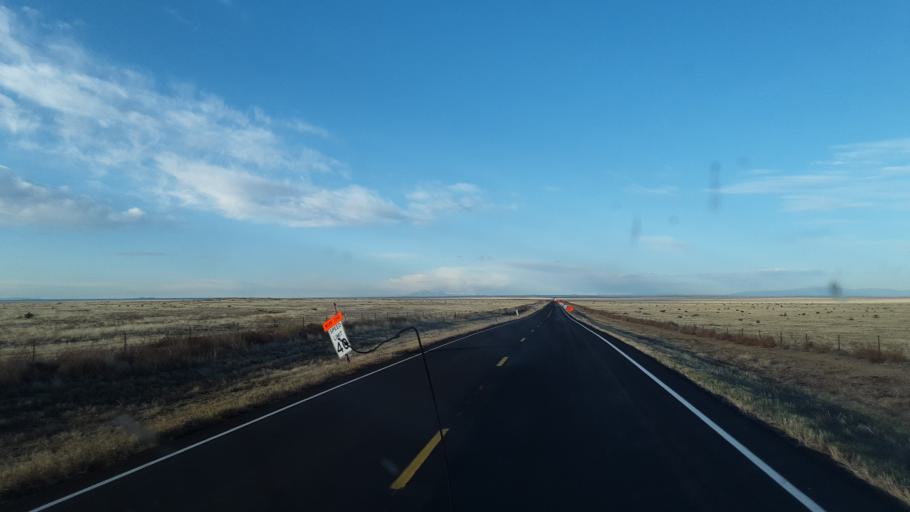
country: US
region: Colorado
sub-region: Otero County
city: Rocky Ford
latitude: 37.9669
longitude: -103.8300
